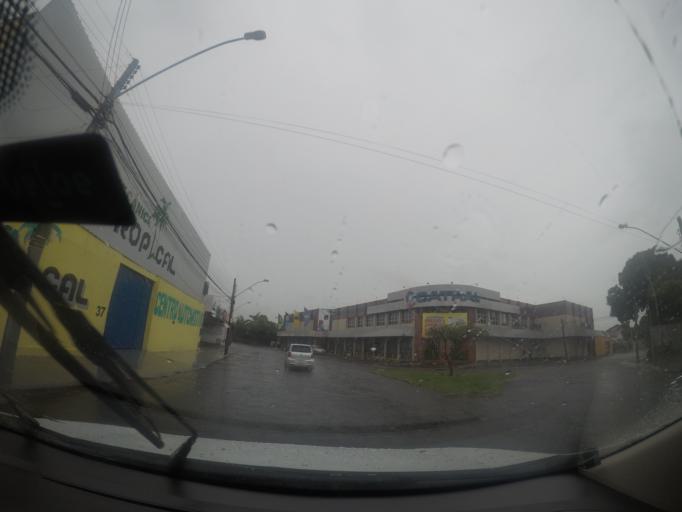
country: BR
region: Goias
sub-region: Goiania
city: Goiania
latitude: -16.6765
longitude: -49.2804
